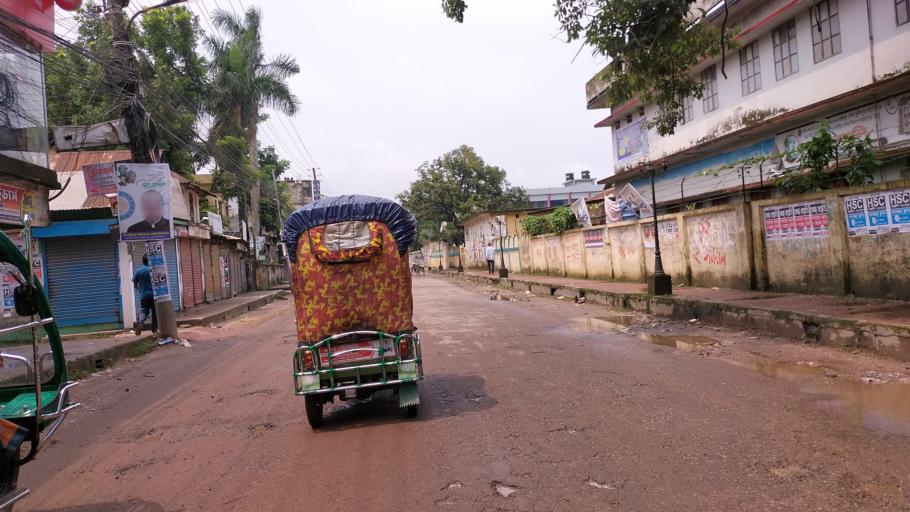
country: BD
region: Dhaka
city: Netrakona
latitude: 24.8768
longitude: 90.7302
